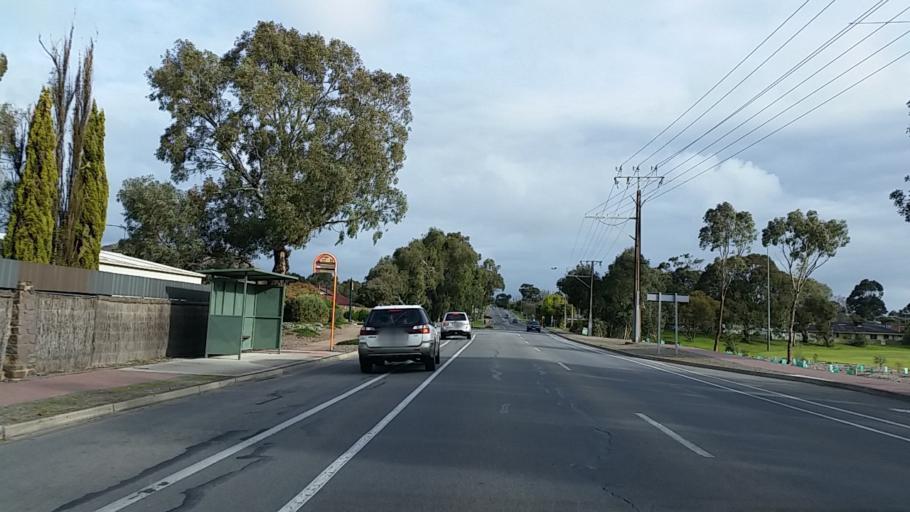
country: AU
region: South Australia
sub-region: Onkaparinga
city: Morphett Vale
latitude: -35.1369
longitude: 138.5372
